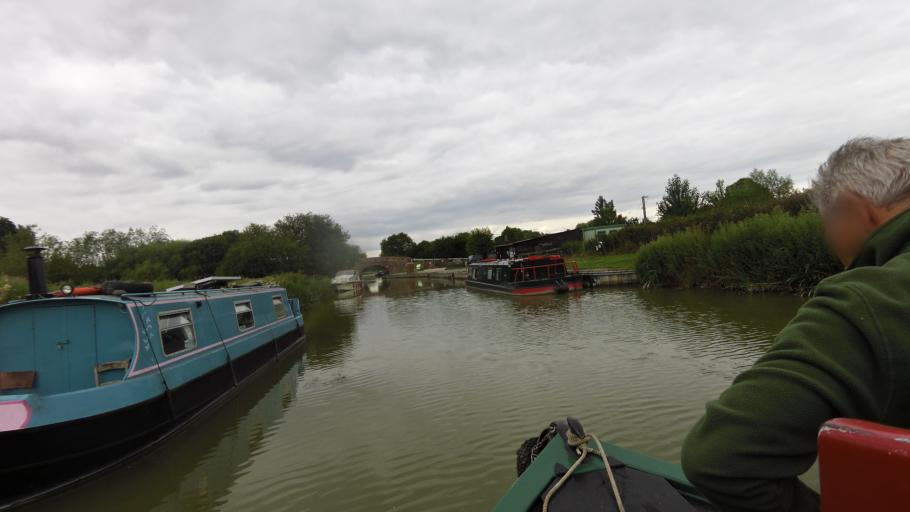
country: GB
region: England
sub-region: Wiltshire
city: Great Bedwyn
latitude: 51.3776
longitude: -1.5993
